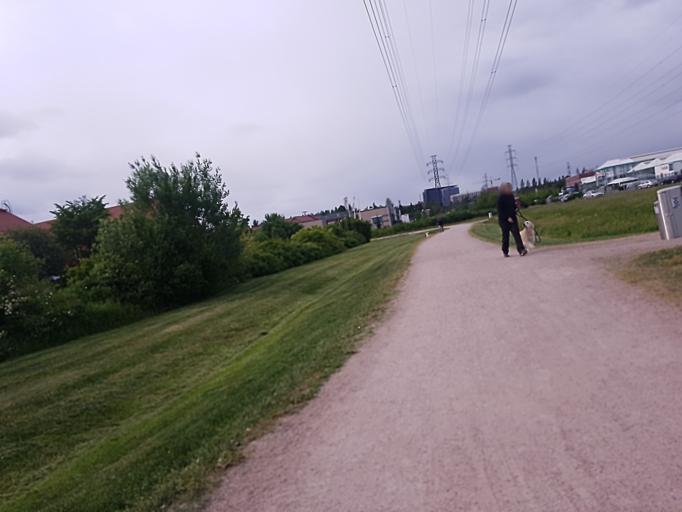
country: FI
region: Uusimaa
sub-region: Helsinki
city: Vantaa
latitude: 60.2801
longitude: 24.9701
